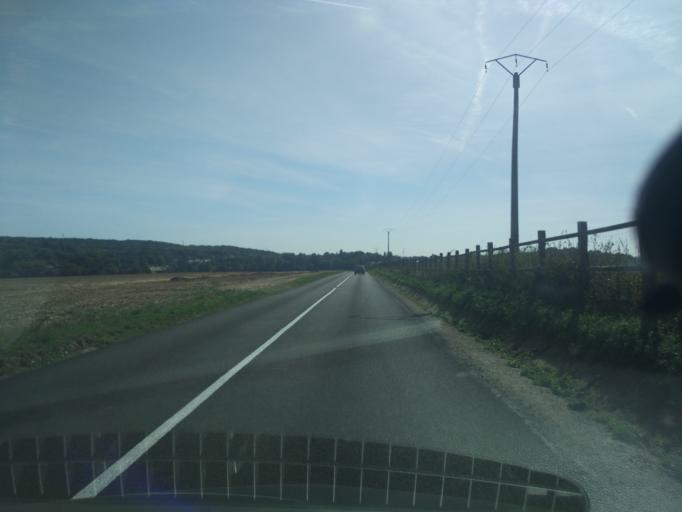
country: FR
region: Ile-de-France
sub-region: Departement de l'Essonne
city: Forges-les-Bains
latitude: 48.6351
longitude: 2.1080
